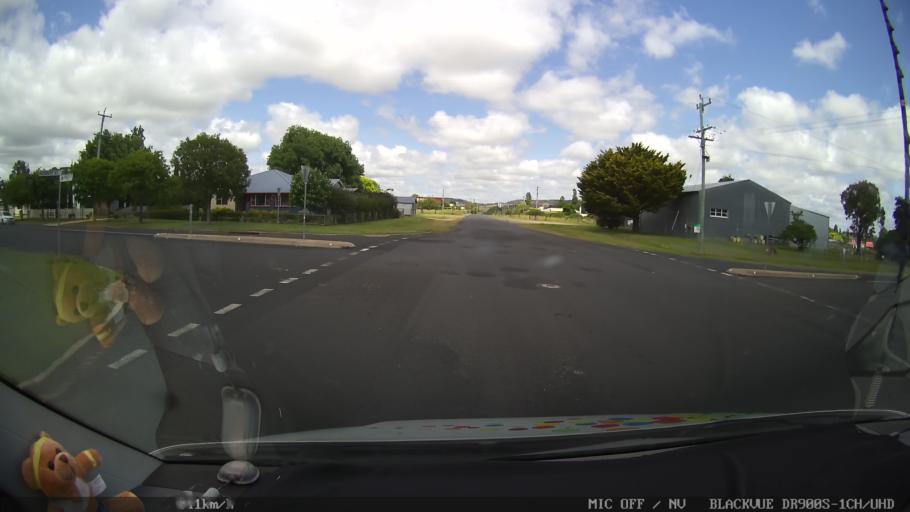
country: AU
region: New South Wales
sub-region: Glen Innes Severn
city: Glen Innes
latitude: -29.7304
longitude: 151.7294
